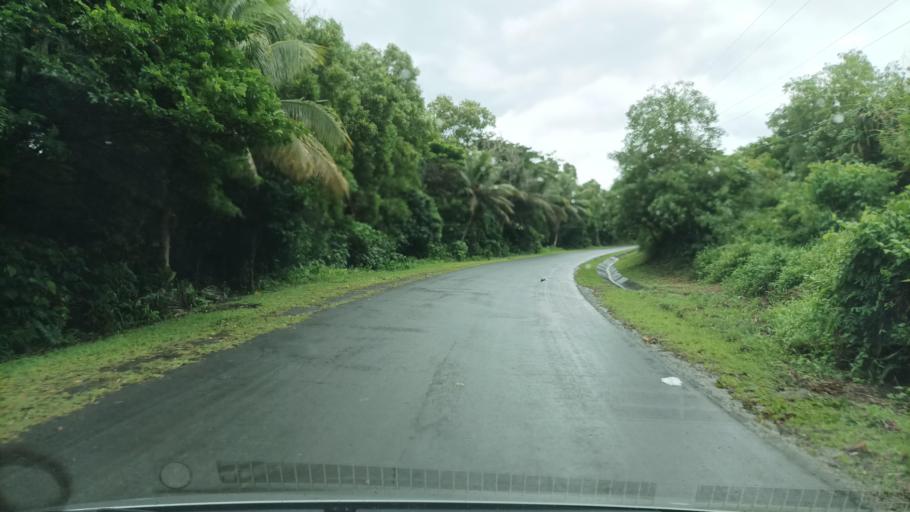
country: FM
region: Yap
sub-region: Rumung Municipality
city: Rumung
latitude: 9.6003
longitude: 138.1678
